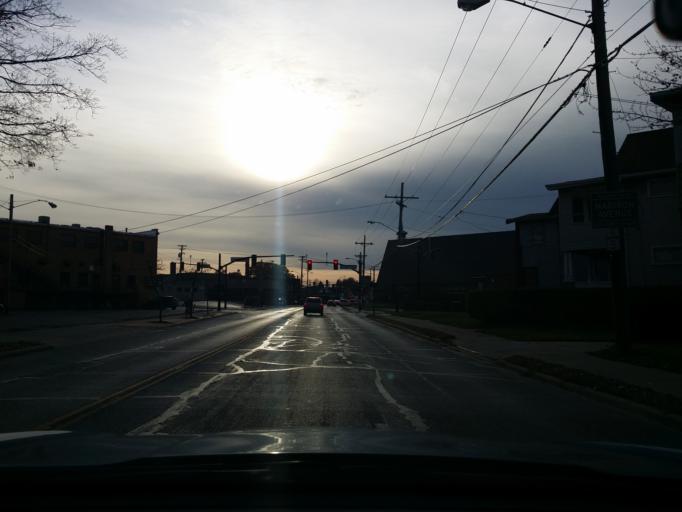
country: US
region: Ohio
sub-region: Cuyahoga County
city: Lakewood
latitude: 41.4782
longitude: -81.8067
